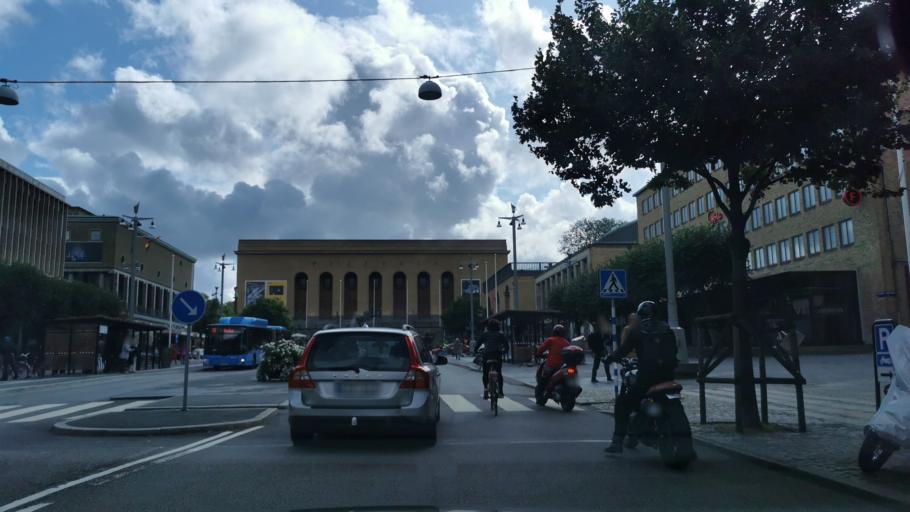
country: SE
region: Vaestra Goetaland
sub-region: Goteborg
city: Goeteborg
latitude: 57.6980
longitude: 11.9784
